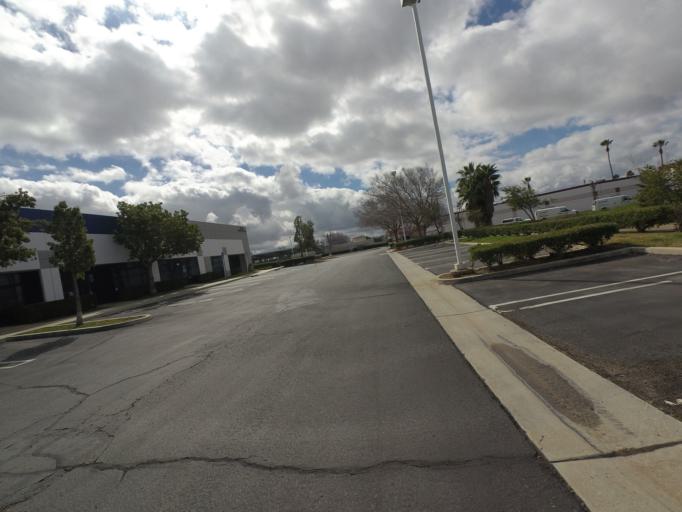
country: US
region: California
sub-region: Riverside County
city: March Air Force Base
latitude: 33.9121
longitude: -117.2684
